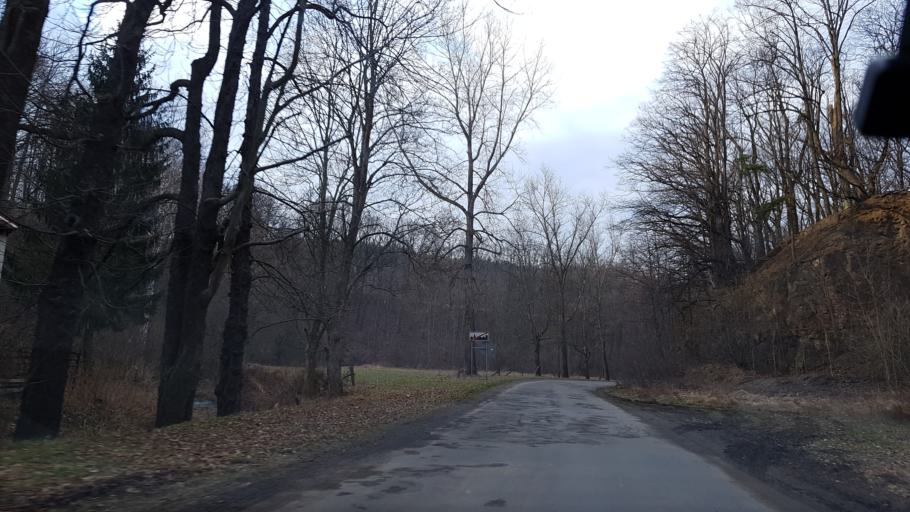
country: PL
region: Lower Silesian Voivodeship
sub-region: Powiat zabkowicki
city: Zloty Stok
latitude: 50.4736
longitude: 16.8093
